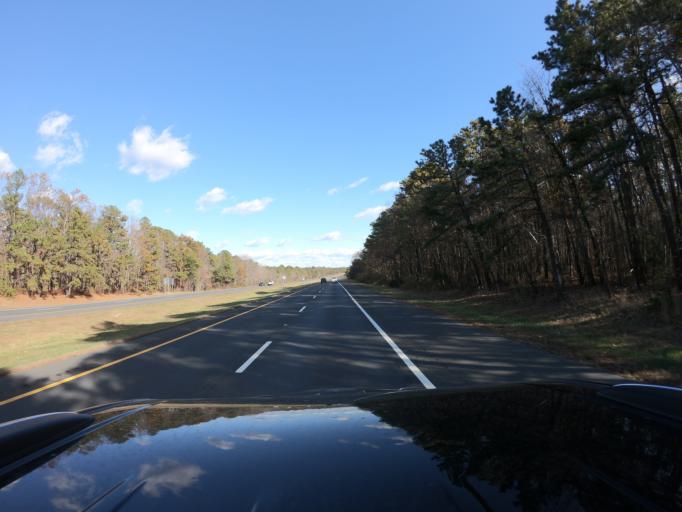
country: US
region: New Jersey
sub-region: Monmouth County
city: Farmingdale
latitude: 40.1671
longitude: -74.1937
